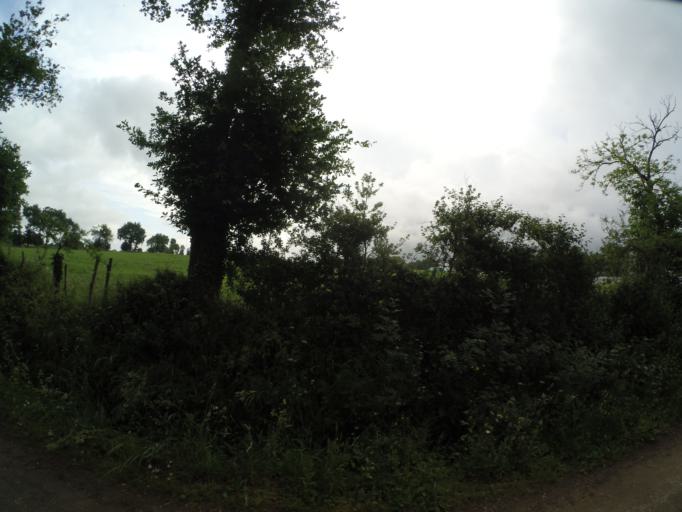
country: FR
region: Pays de la Loire
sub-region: Departement de la Vendee
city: Nesmy
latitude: 46.6091
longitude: -1.3944
